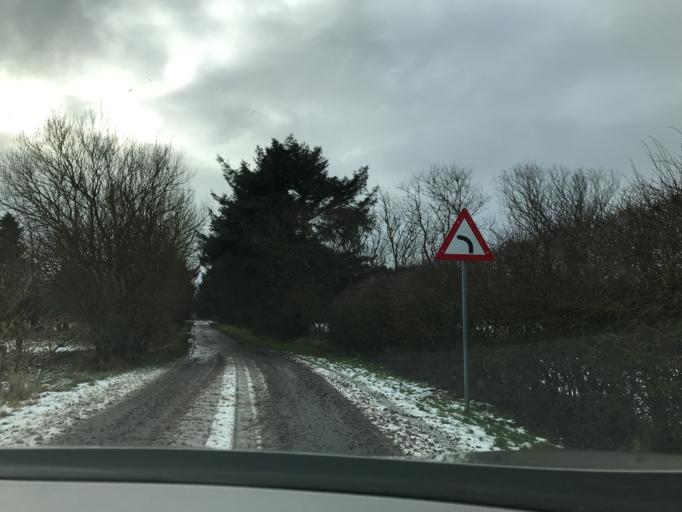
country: DK
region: South Denmark
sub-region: Varde Kommune
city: Oksbol
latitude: 55.7616
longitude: 8.2704
